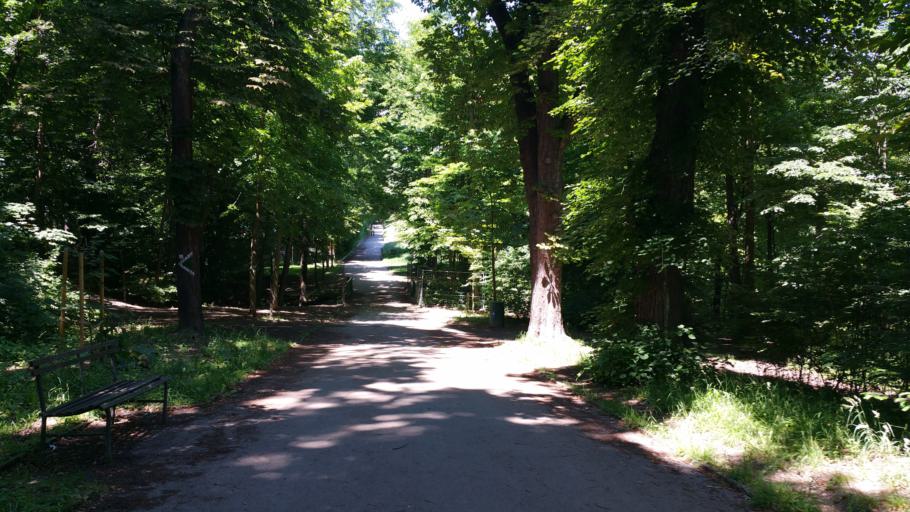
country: AT
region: Lower Austria
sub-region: Politischer Bezirk Wien-Umgebung
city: Klosterneuburg
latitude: 48.2387
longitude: 16.2812
